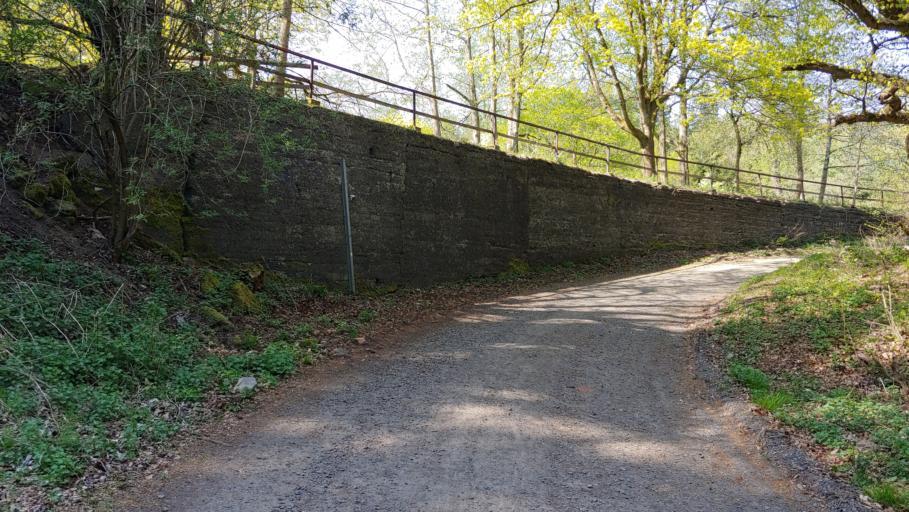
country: DE
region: Hesse
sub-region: Regierungsbezirk Kassel
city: Baunatal
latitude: 51.3108
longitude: 9.3607
